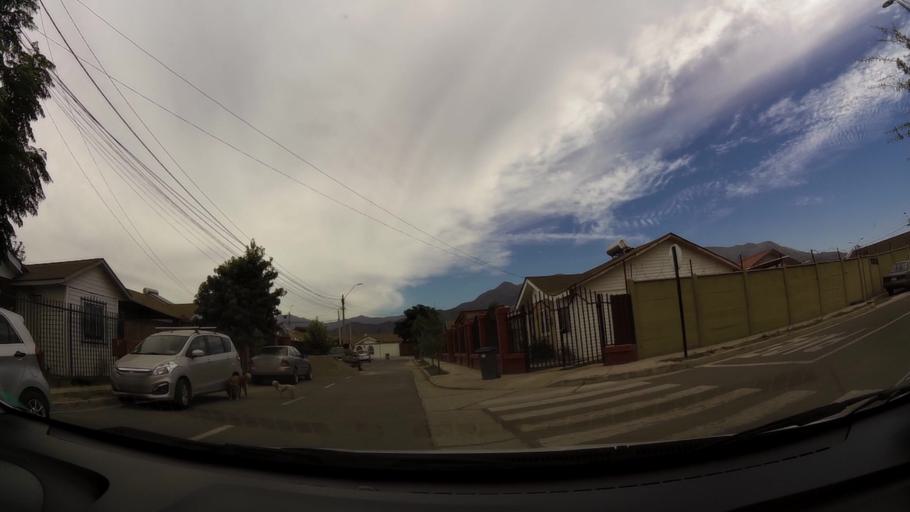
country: CL
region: O'Higgins
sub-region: Provincia de Cachapoal
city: Graneros
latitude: -34.0817
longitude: -70.7397
